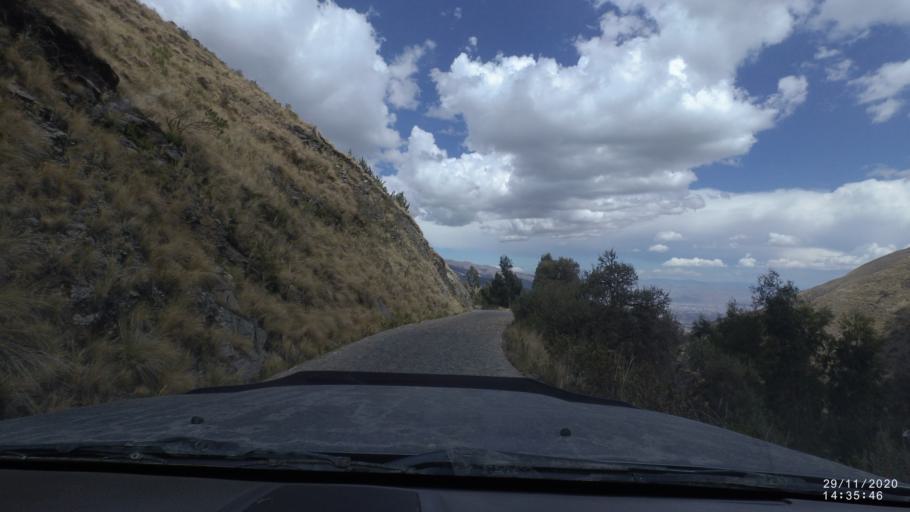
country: BO
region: Cochabamba
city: Sipe Sipe
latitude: -17.2717
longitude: -66.3343
